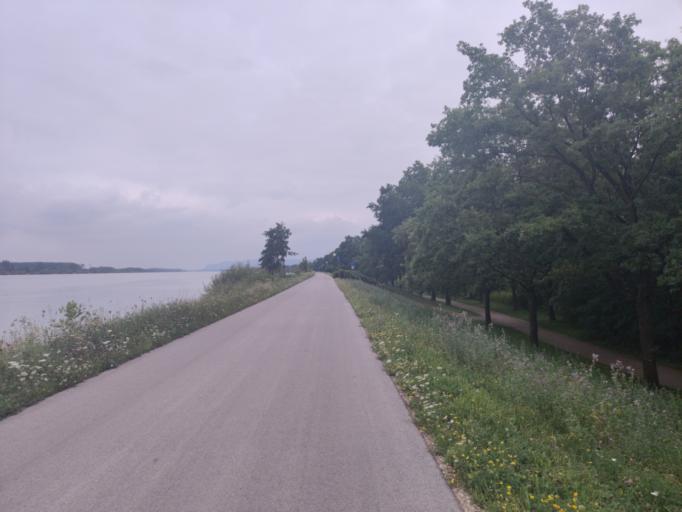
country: AT
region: Lower Austria
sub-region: Politischer Bezirk Tulln
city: Tulln
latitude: 48.3326
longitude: 16.0956
